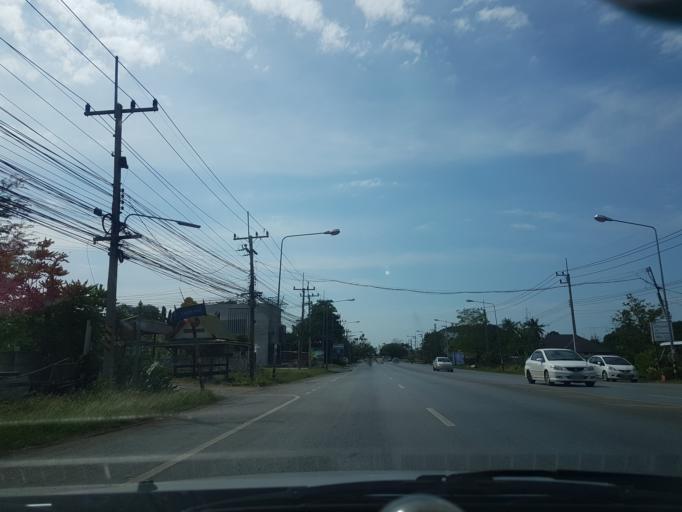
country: TH
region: Lop Buri
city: Lop Buri
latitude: 14.7993
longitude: 100.7164
